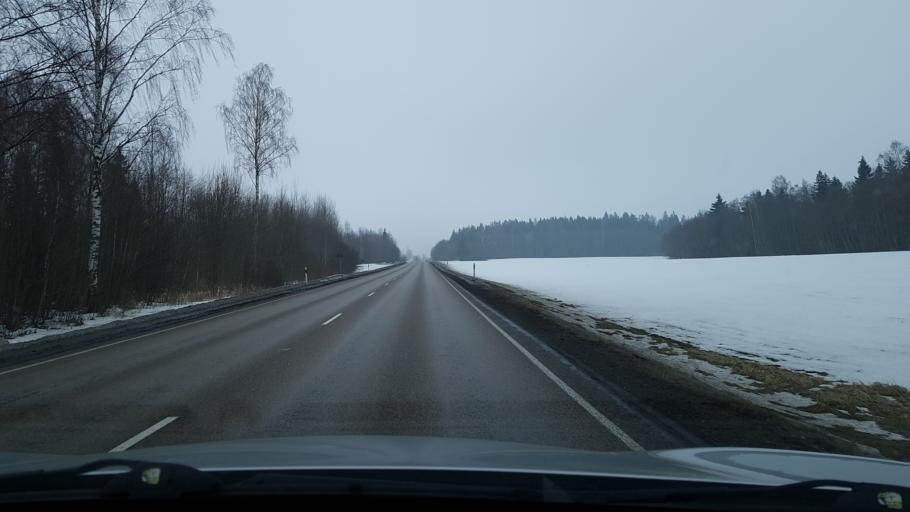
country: EE
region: Tartu
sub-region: Elva linn
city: Elva
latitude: 58.1005
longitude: 26.2320
